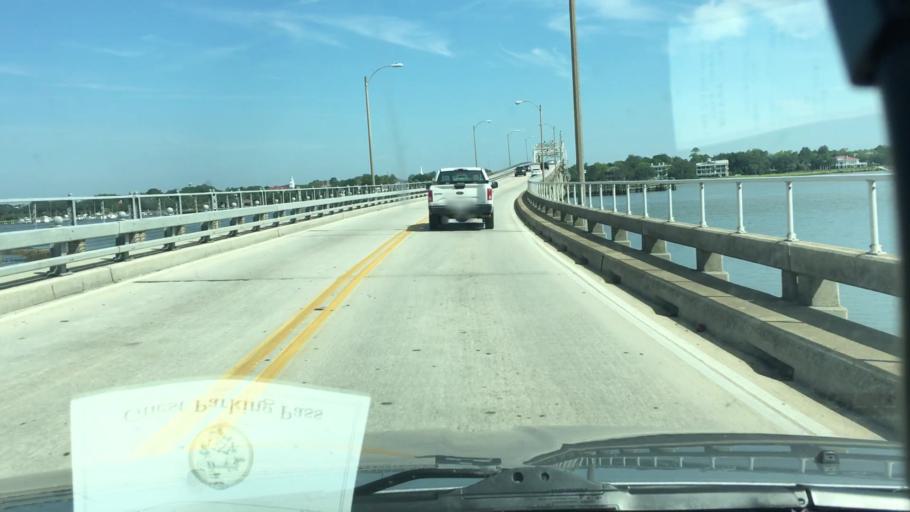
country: US
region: South Carolina
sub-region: Beaufort County
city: Beaufort
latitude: 32.4243
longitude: -80.6683
